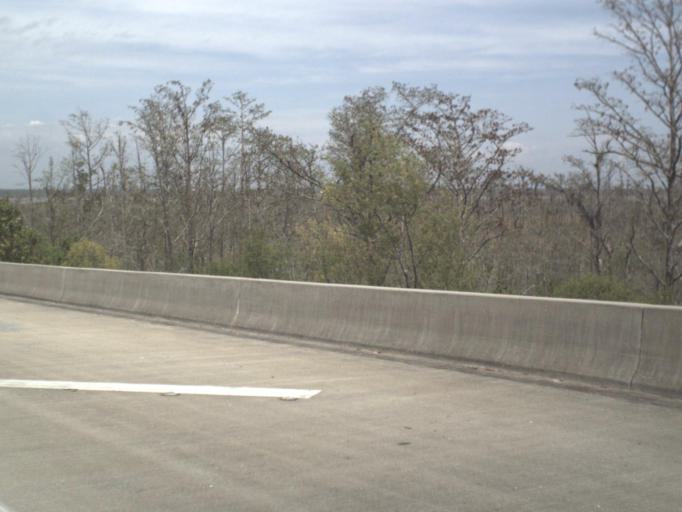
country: US
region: Florida
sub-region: Escambia County
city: Ferry Pass
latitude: 30.5514
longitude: -87.1943
